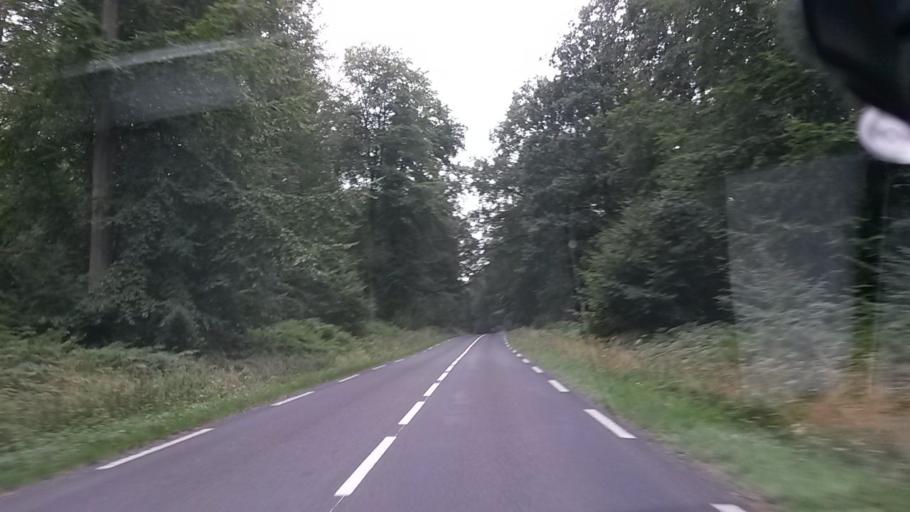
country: FR
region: Haute-Normandie
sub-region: Departement de l'Eure
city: Charleval
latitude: 49.3791
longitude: 1.4675
